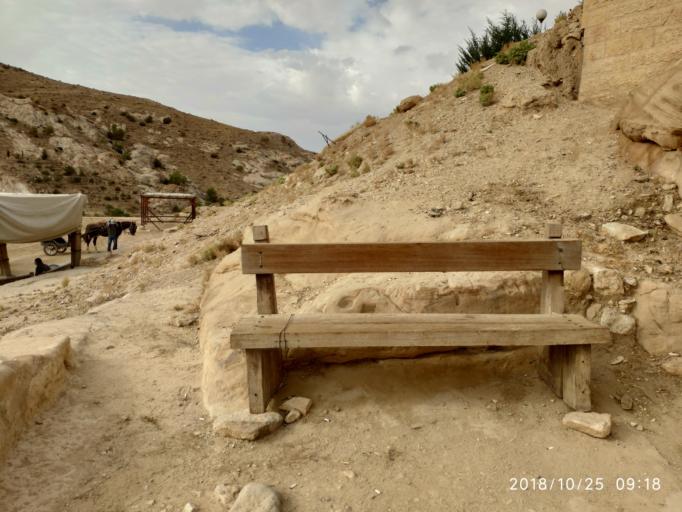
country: JO
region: Ma'an
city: Petra
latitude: 30.3231
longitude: 35.4673
